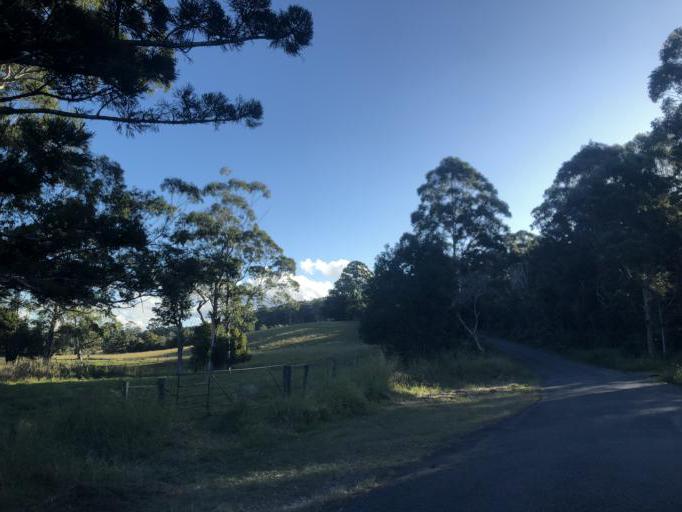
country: AU
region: New South Wales
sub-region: Nambucca Shire
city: Nambucca
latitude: -30.5829
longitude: 152.9441
